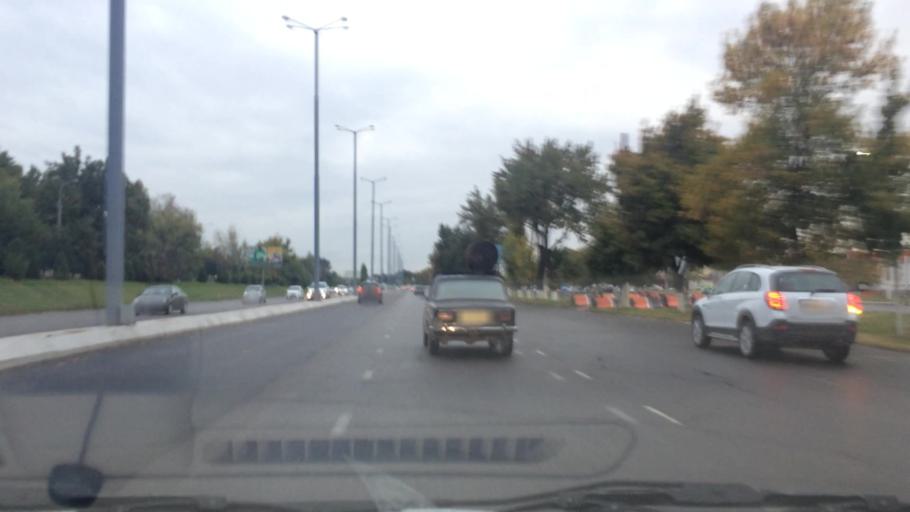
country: UZ
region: Toshkent Shahri
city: Tashkent
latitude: 41.2490
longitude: 69.1809
